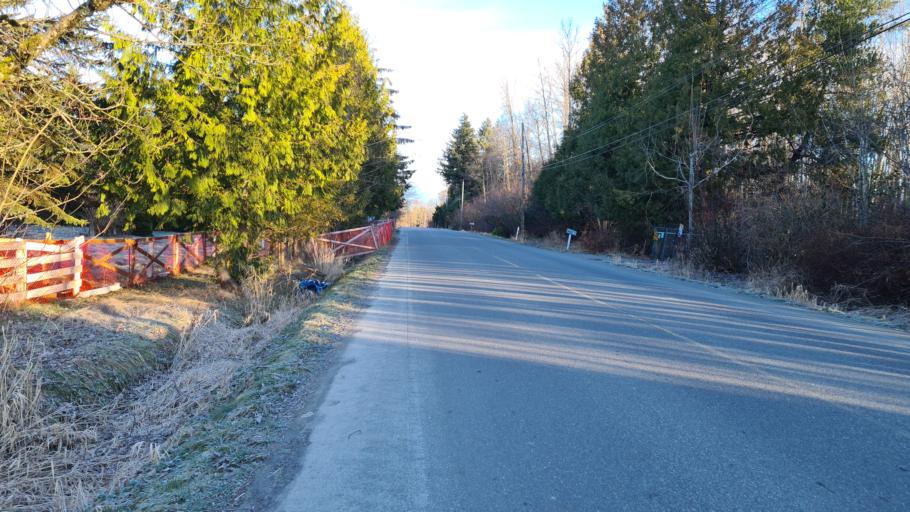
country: CA
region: British Columbia
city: Langley
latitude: 49.1372
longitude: -122.6723
